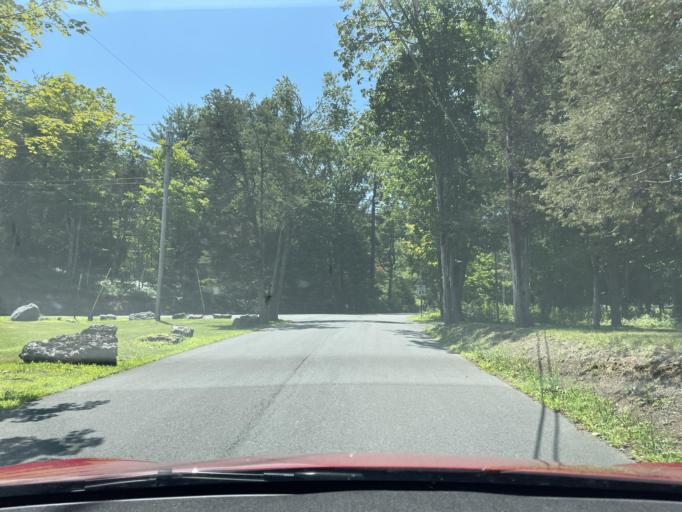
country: US
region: New York
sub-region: Ulster County
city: Lake Katrine
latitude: 41.9998
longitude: -73.9826
